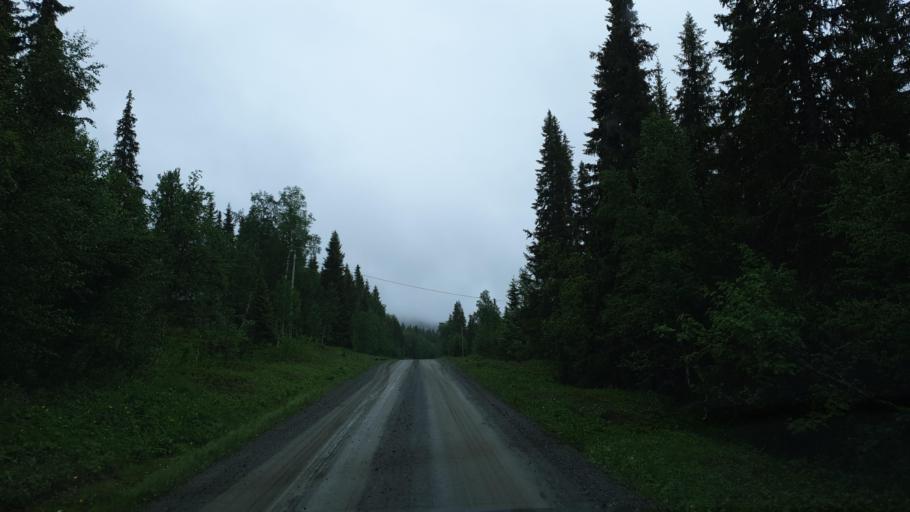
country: SE
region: Vaesterbotten
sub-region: Vilhelmina Kommun
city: Sjoberg
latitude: 65.3445
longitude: 15.8746
